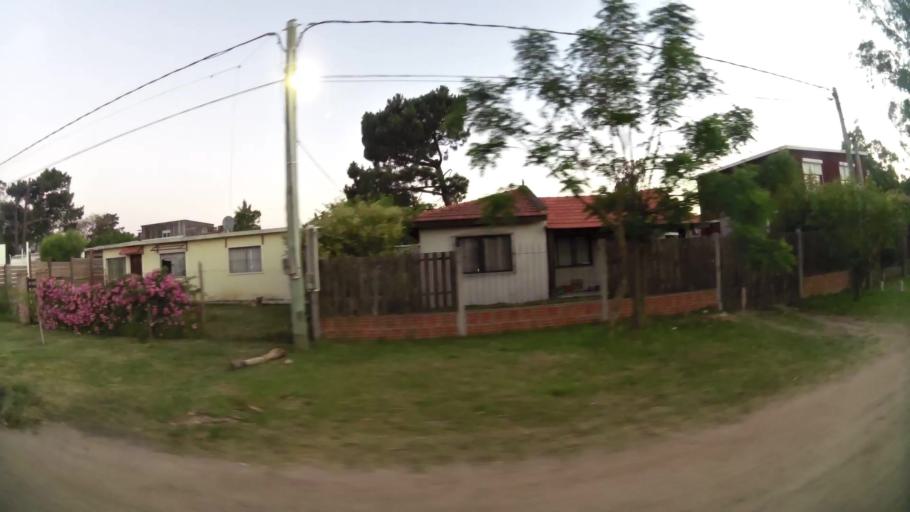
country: UY
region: Canelones
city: Colonia Nicolich
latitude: -34.8186
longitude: -55.9629
